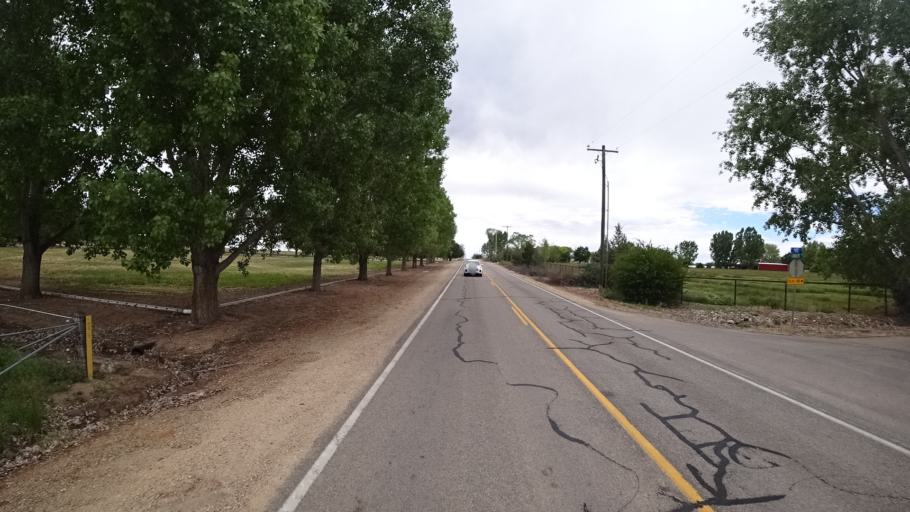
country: US
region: Idaho
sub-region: Ada County
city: Meridian
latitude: 43.5574
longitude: -116.4138
